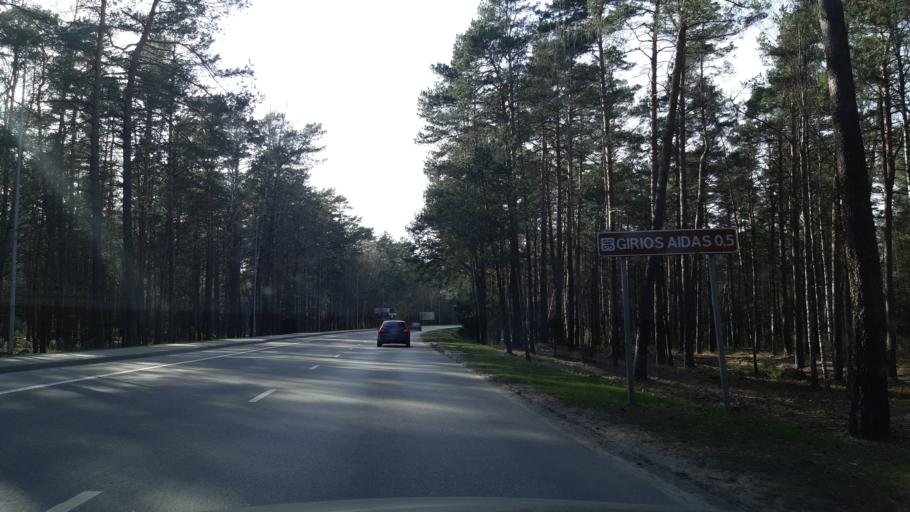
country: LT
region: Alytaus apskritis
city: Druskininkai
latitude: 54.0048
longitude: 24.0110
